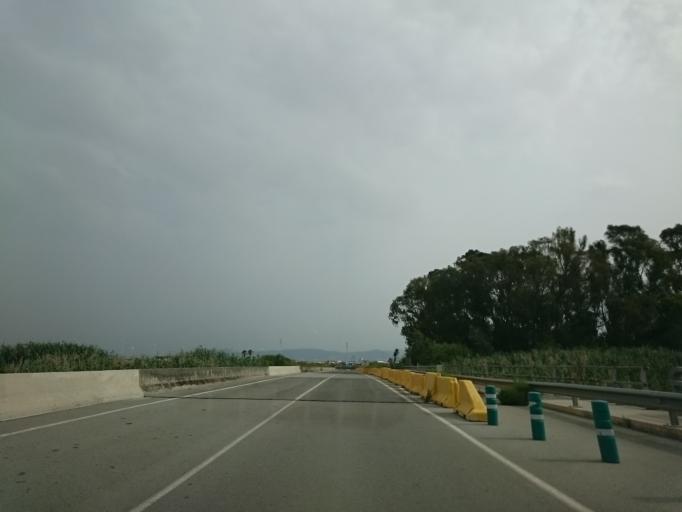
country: ES
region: Catalonia
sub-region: Provincia de Barcelona
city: Viladecans
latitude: 41.2850
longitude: 2.0537
